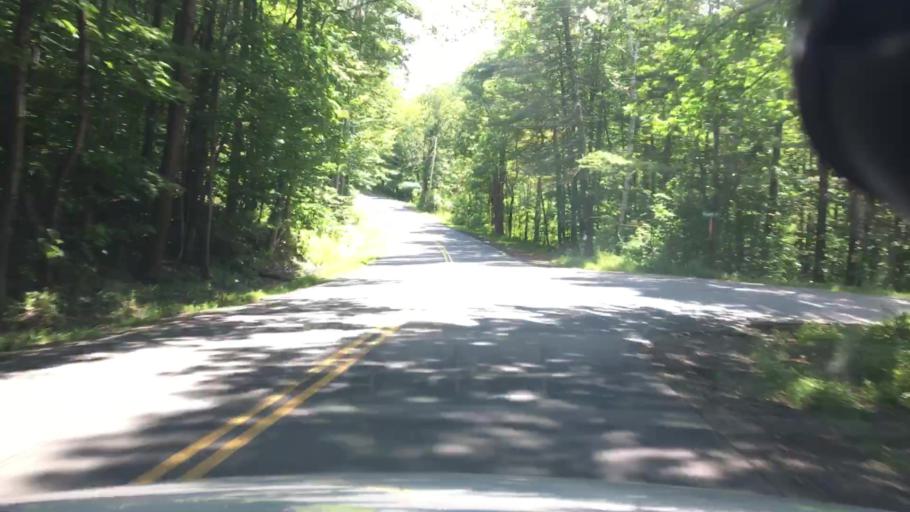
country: US
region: Maine
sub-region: Somerset County
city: Skowhegan
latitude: 44.7240
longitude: -69.7040
